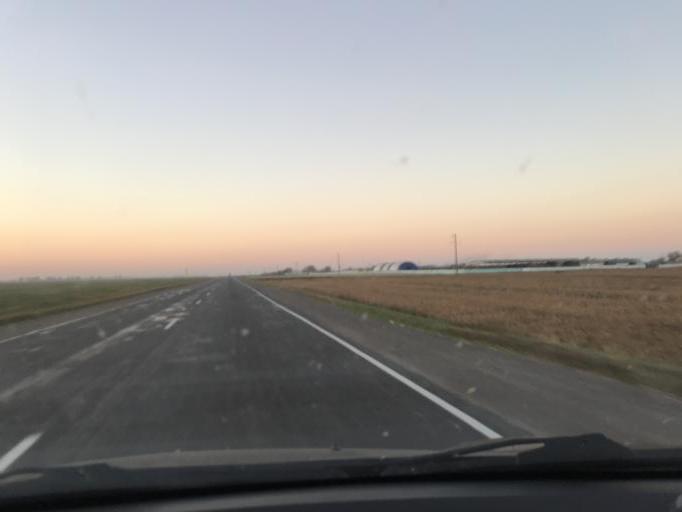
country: BY
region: Gomel
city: Horad Rechytsa
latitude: 52.2439
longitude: 30.5005
